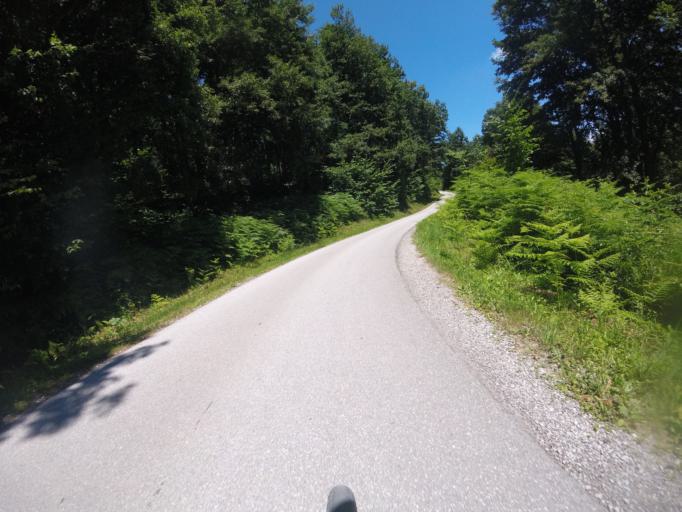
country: SI
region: Metlika
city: Metlika
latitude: 45.7142
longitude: 15.3863
